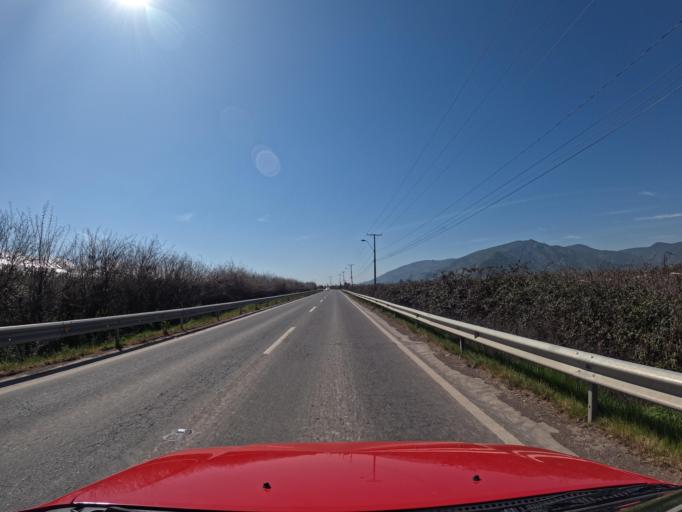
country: CL
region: Maule
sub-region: Provincia de Curico
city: Rauco
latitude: -35.0321
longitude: -71.4425
